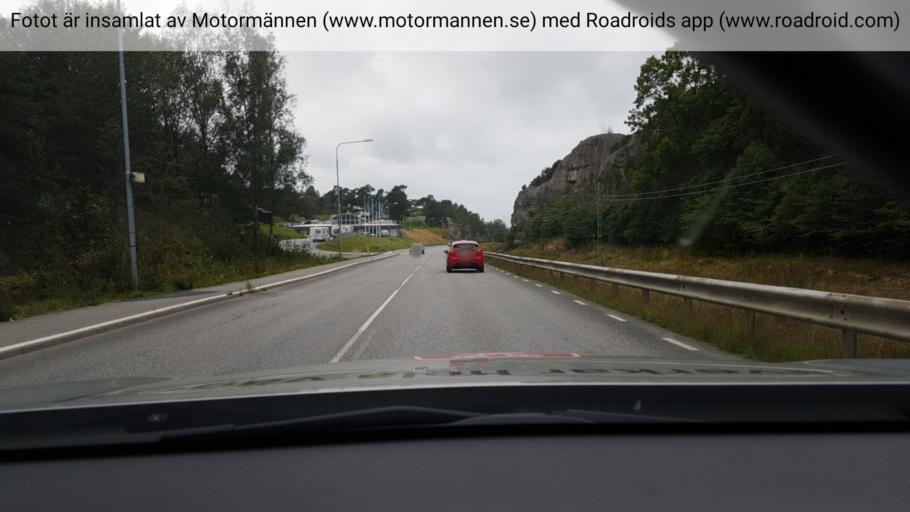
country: SE
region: Vaestra Goetaland
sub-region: Stromstads Kommun
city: Stroemstad
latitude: 58.9314
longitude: 11.1833
